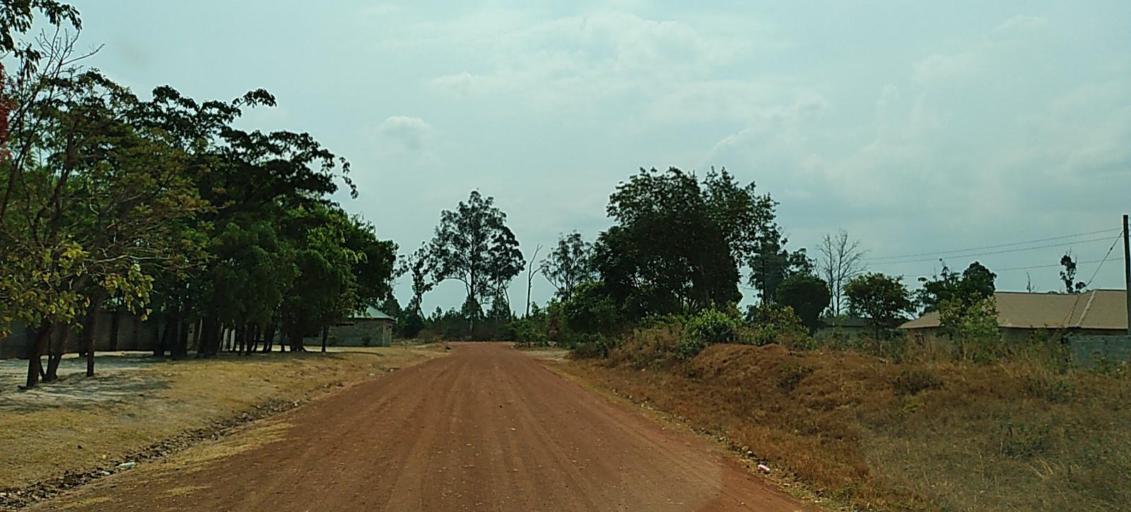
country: ZM
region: Copperbelt
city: Kalulushi
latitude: -12.8325
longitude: 28.0789
